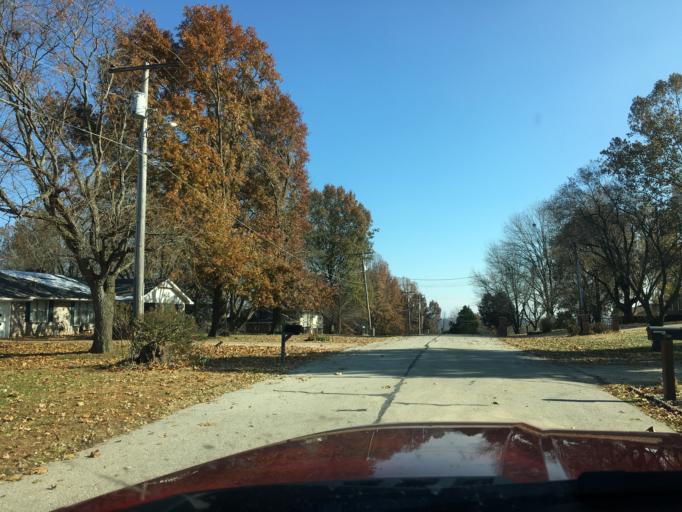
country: US
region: Missouri
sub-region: Cole County
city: Wardsville
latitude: 38.4857
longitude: -92.1748
